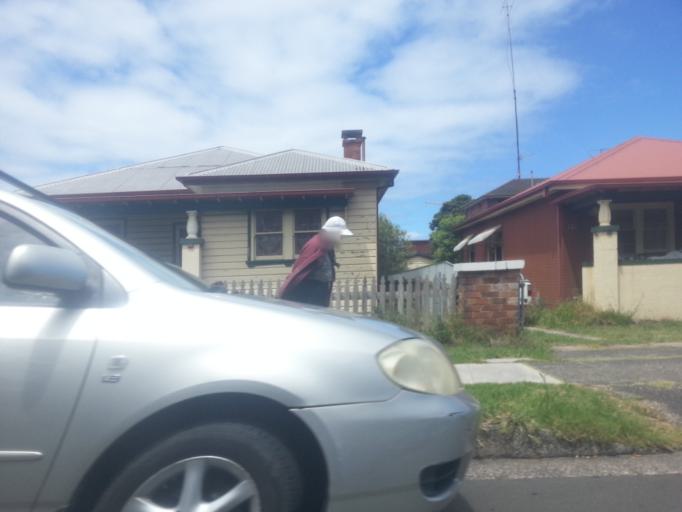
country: AU
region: New South Wales
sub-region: Wollongong
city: Wollongong
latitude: -34.4285
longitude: 150.8946
